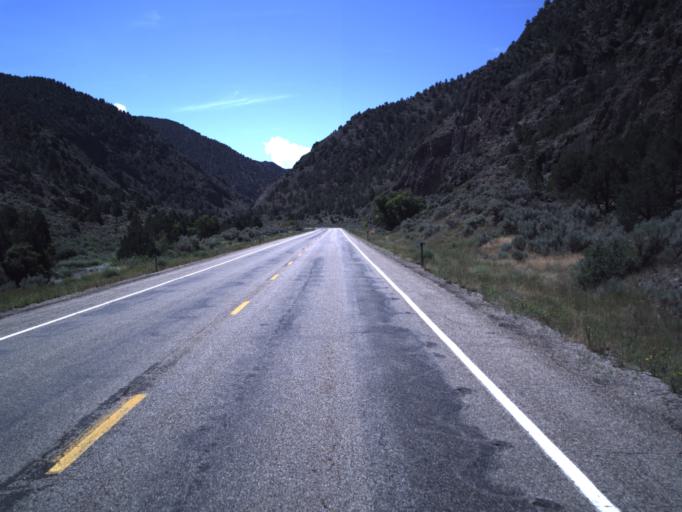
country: US
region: Utah
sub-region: Piute County
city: Junction
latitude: 38.1155
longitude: -112.3382
